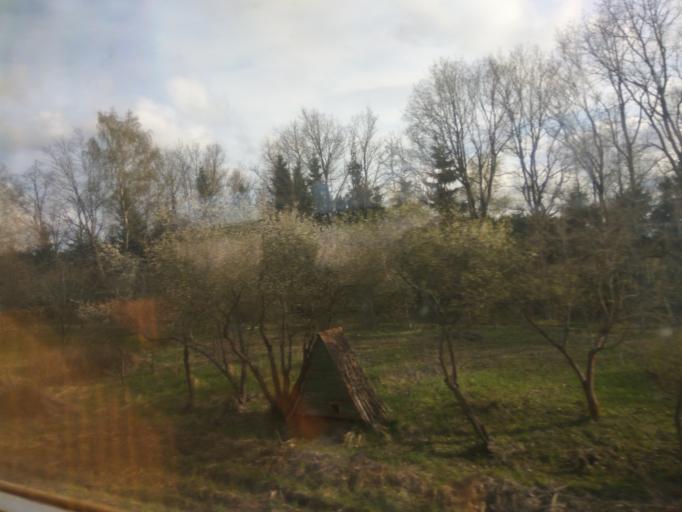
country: LV
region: Babite
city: Pinki
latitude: 56.9638
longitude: 23.9212
